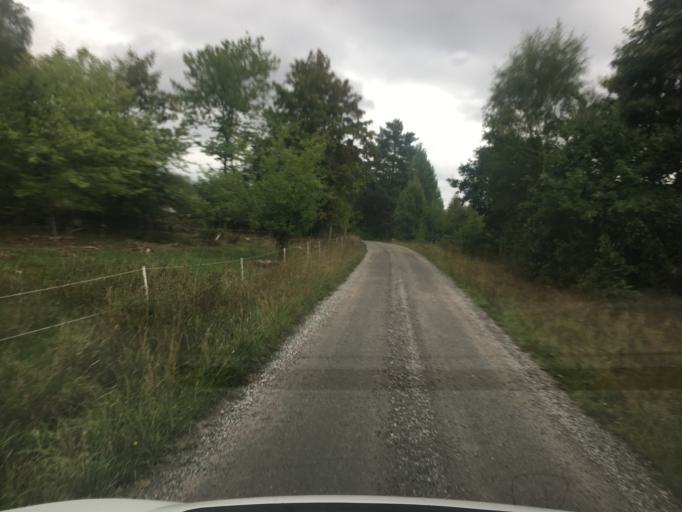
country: SE
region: Kronoberg
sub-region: Ljungby Kommun
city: Lagan
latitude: 56.9563
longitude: 14.0412
